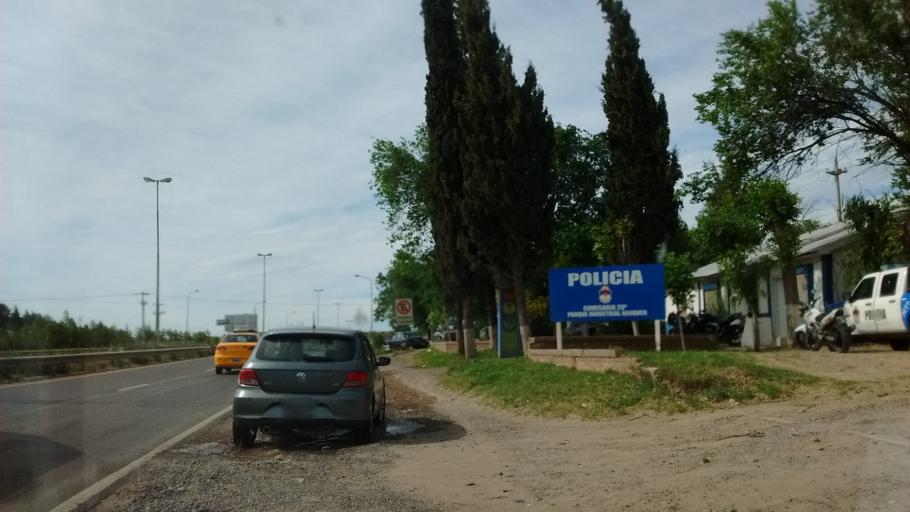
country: AR
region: Neuquen
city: Neuquen
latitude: -38.9110
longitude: -68.0808
